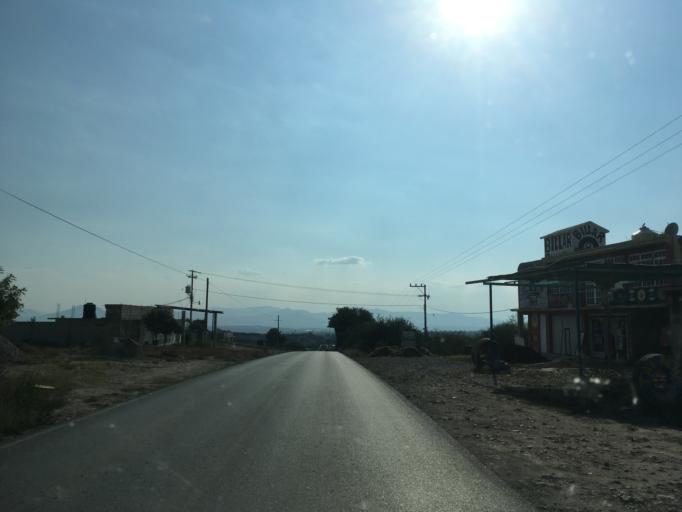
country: MX
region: Hidalgo
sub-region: Ixmiquilpan
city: El Nith
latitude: 20.5600
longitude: -99.1552
